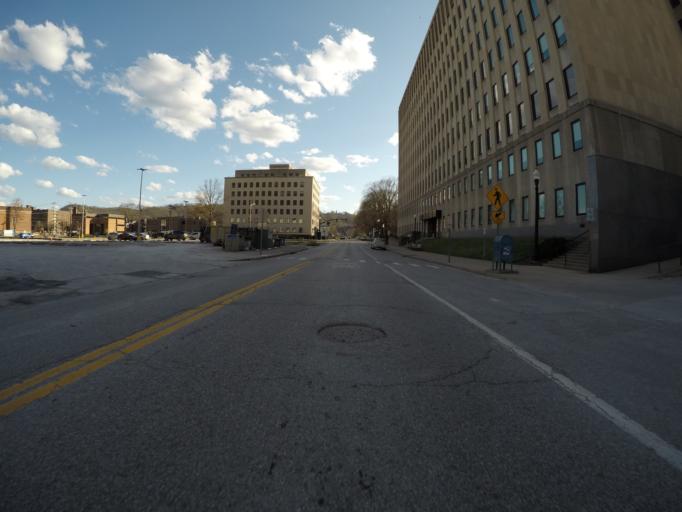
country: US
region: West Virginia
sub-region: Kanawha County
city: Charleston
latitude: 38.3381
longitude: -81.6098
